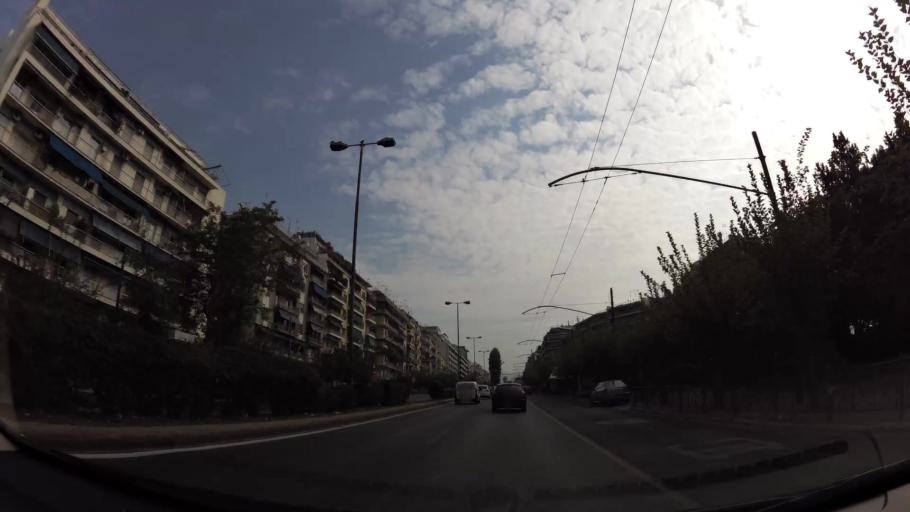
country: GR
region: Attica
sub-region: Nomarchia Athinas
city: Kipseli
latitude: 37.9897
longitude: 23.7440
